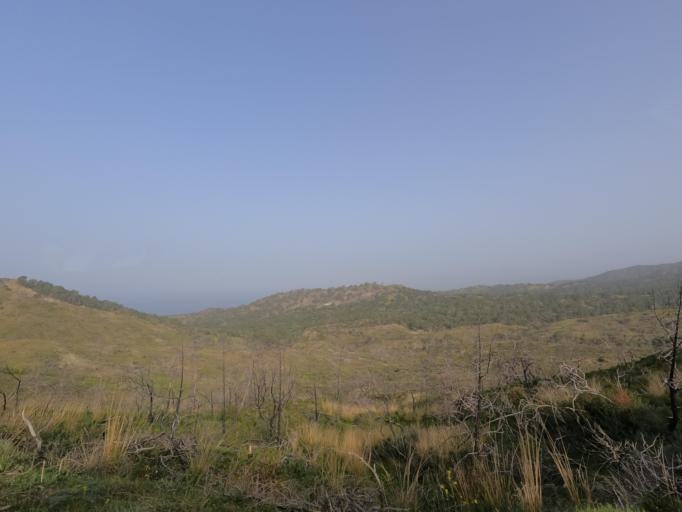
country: CY
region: Pafos
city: Polis
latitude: 34.9969
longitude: 32.3341
